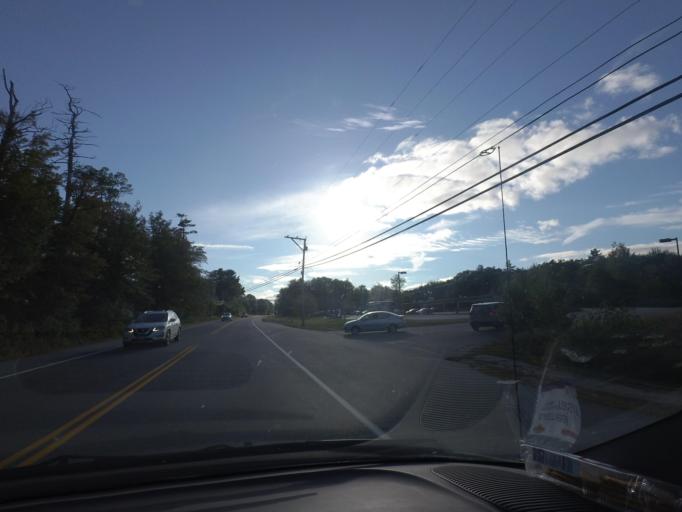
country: US
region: New Hampshire
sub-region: Strafford County
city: Rochester
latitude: 43.3270
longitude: -70.9519
